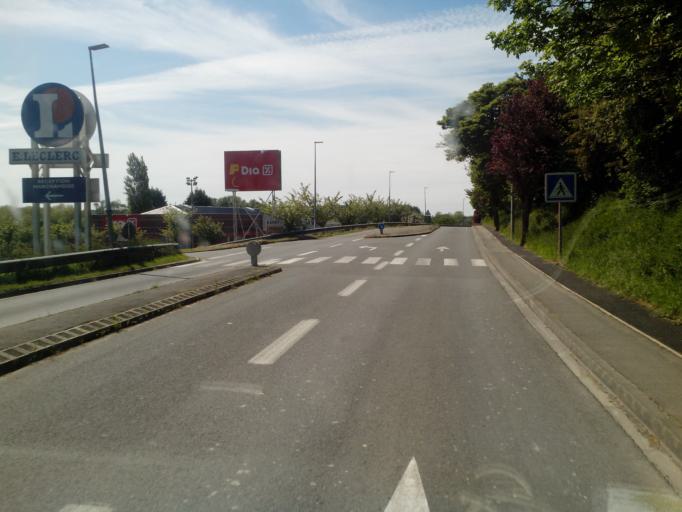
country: FR
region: Nord-Pas-de-Calais
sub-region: Departement du Pas-de-Calais
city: Montreuil
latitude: 50.4831
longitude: 1.7565
